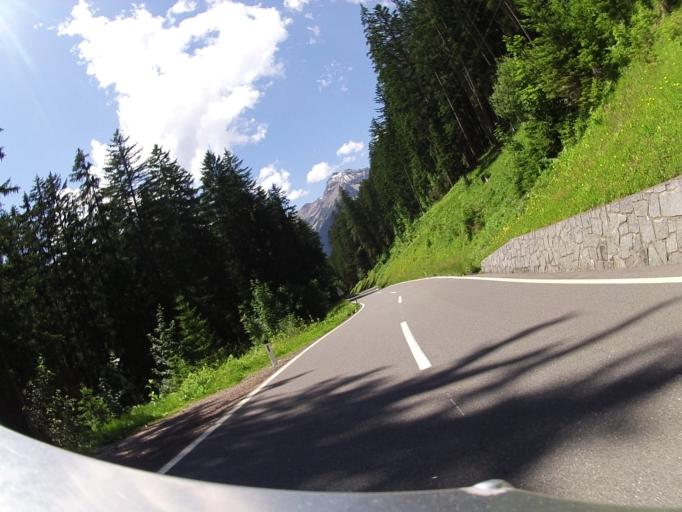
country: AT
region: Tyrol
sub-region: Politischer Bezirk Reutte
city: Elmen
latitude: 47.3154
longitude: 10.5617
